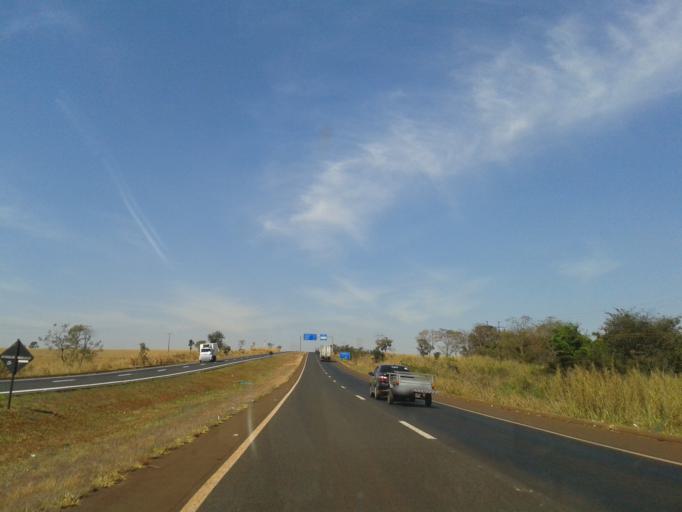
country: BR
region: Goias
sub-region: Itumbiara
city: Itumbiara
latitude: -18.2590
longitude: -49.2492
